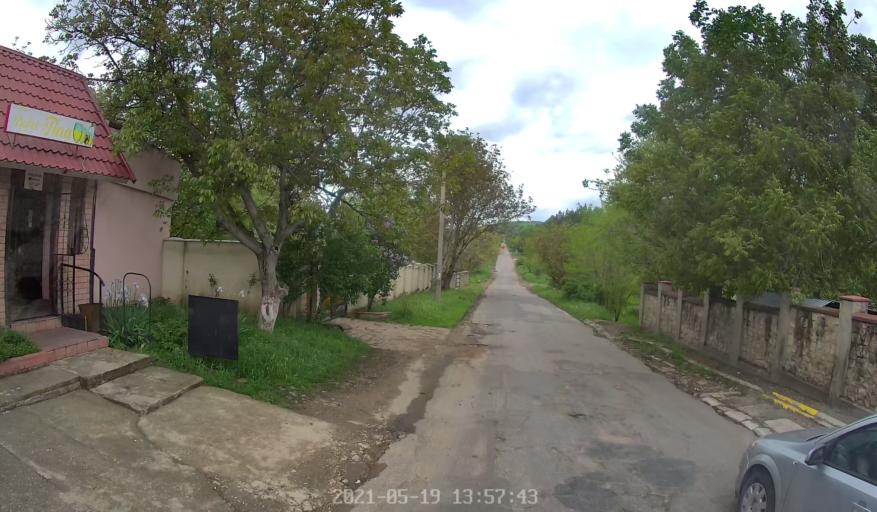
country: MD
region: Chisinau
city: Chisinau
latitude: 47.0399
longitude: 28.9093
